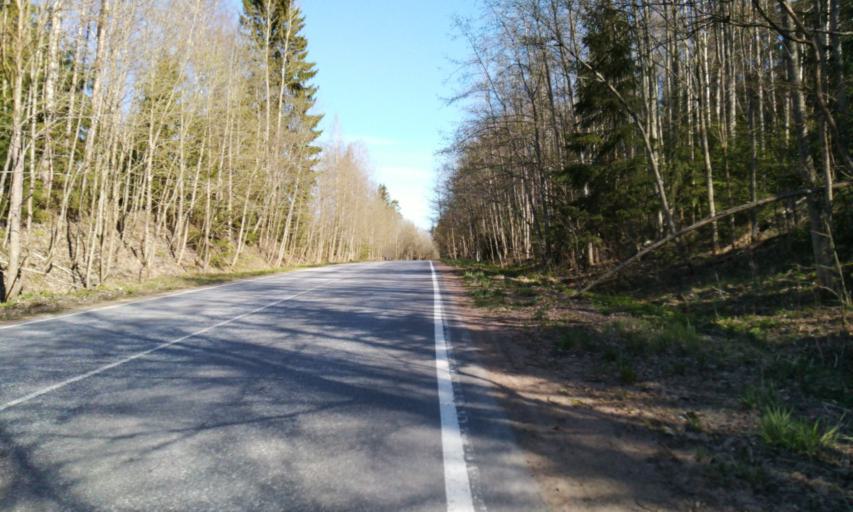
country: RU
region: Leningrad
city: Garbolovo
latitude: 60.3619
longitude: 30.4441
